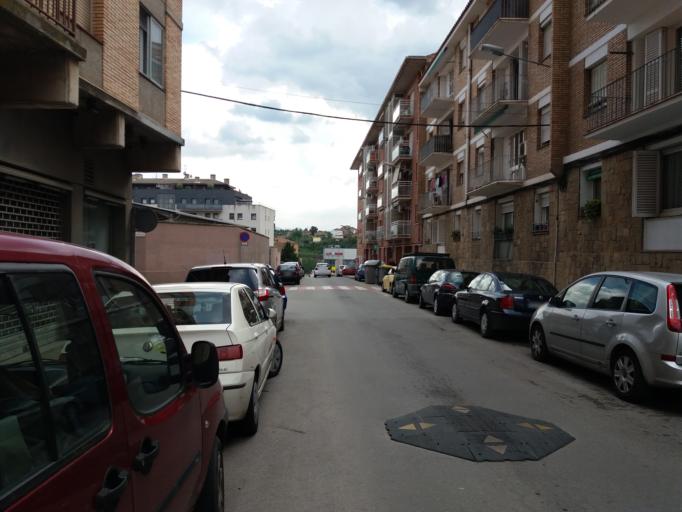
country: ES
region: Catalonia
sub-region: Provincia de Barcelona
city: Manresa
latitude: 41.7250
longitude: 1.8179
